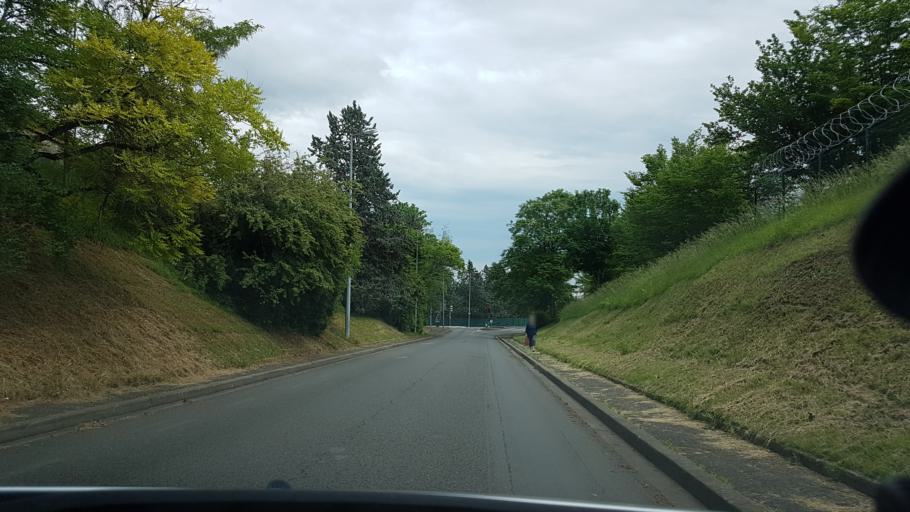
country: FR
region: Centre
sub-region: Departement du Cher
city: Bourges
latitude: 47.0954
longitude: 2.4004
